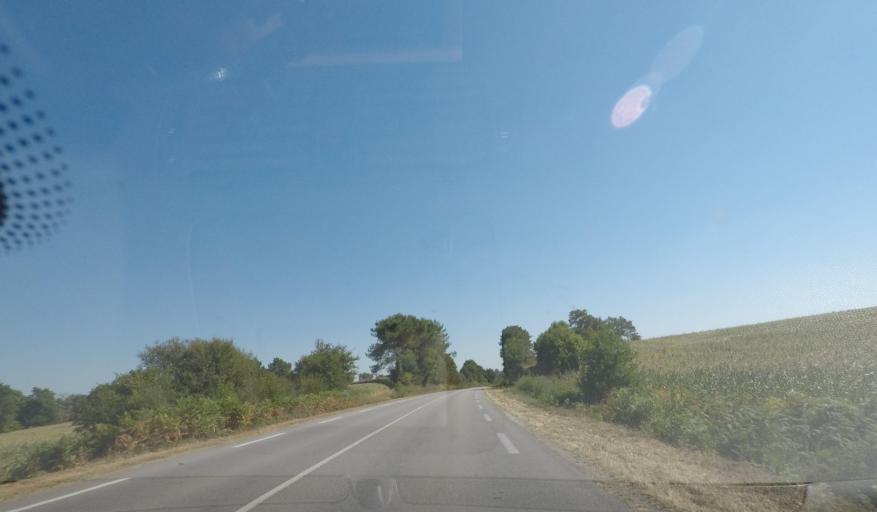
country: FR
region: Brittany
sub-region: Departement du Morbihan
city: Peaule
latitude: 47.6043
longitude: -2.3839
